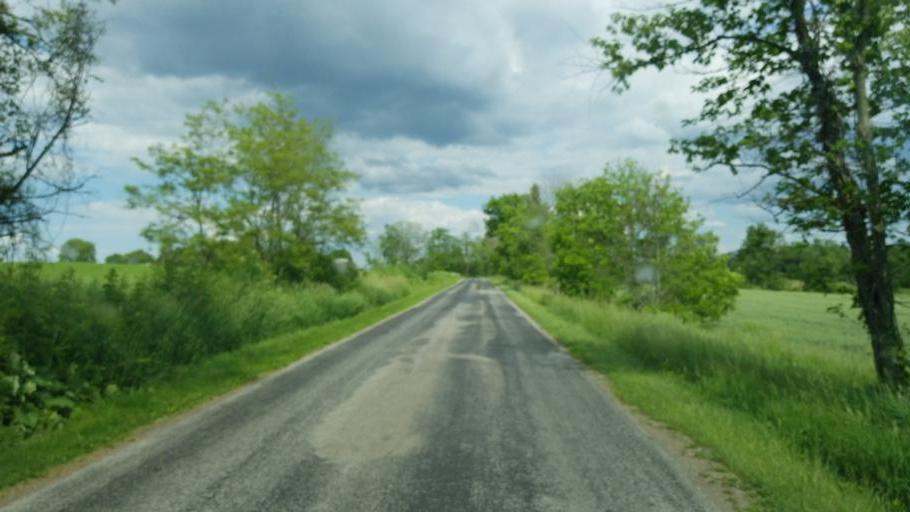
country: US
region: Ohio
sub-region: Huron County
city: Greenwich
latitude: 40.9339
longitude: -82.5455
